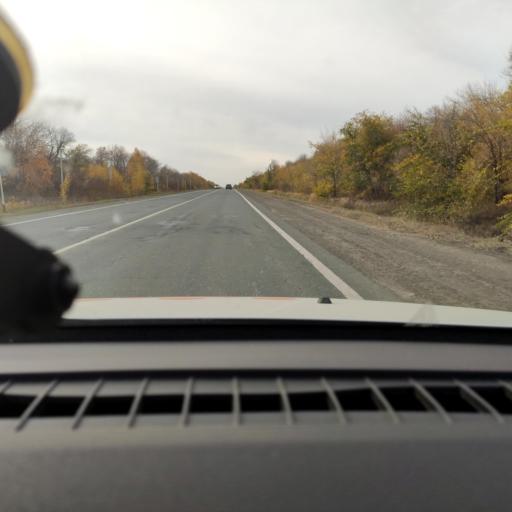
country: RU
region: Samara
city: Novokuybyshevsk
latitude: 52.9856
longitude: 49.8686
